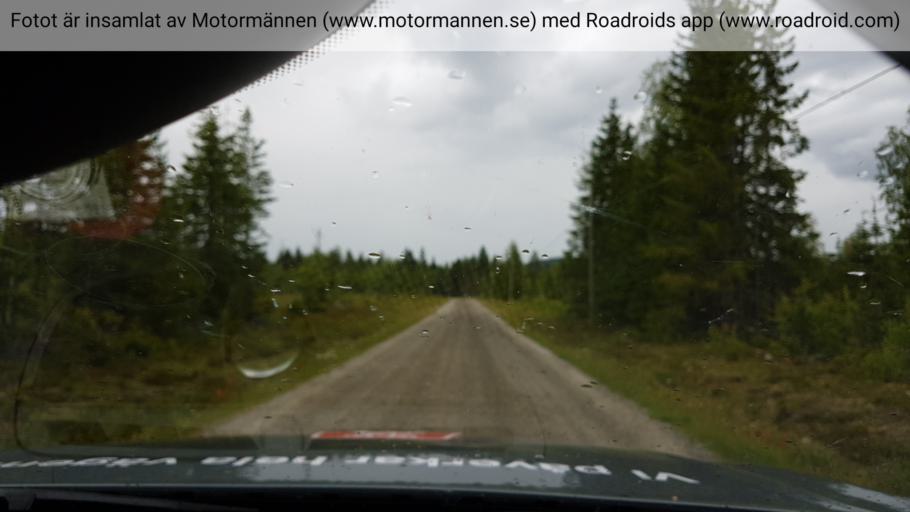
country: SE
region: Jaemtland
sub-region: Bergs Kommun
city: Hoverberg
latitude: 62.5024
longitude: 14.7034
